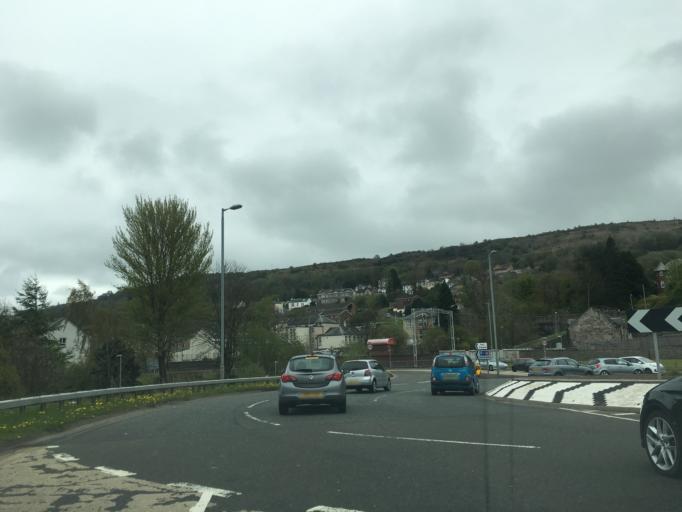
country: GB
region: Scotland
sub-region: Inverclyde
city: Port Glasgow
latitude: 55.9365
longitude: -4.7022
